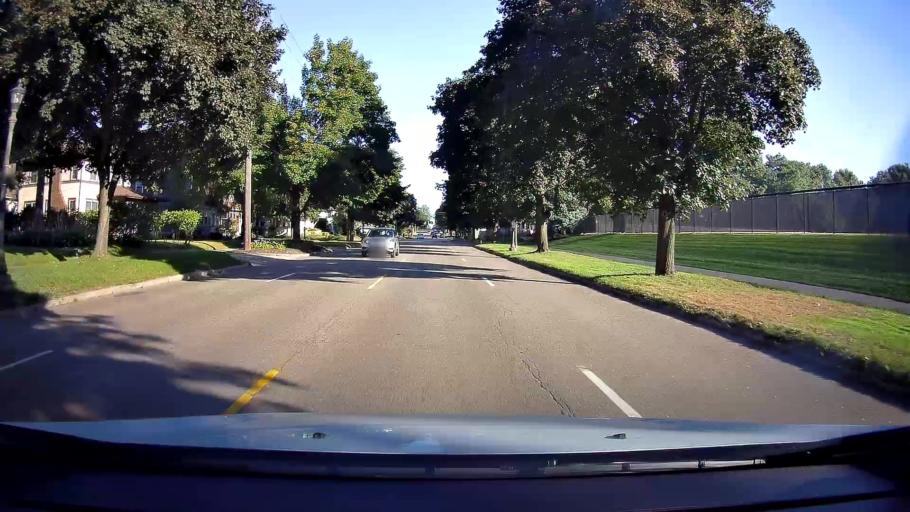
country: US
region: Minnesota
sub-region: Ramsey County
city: Falcon Heights
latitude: 44.9455
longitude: -93.1924
